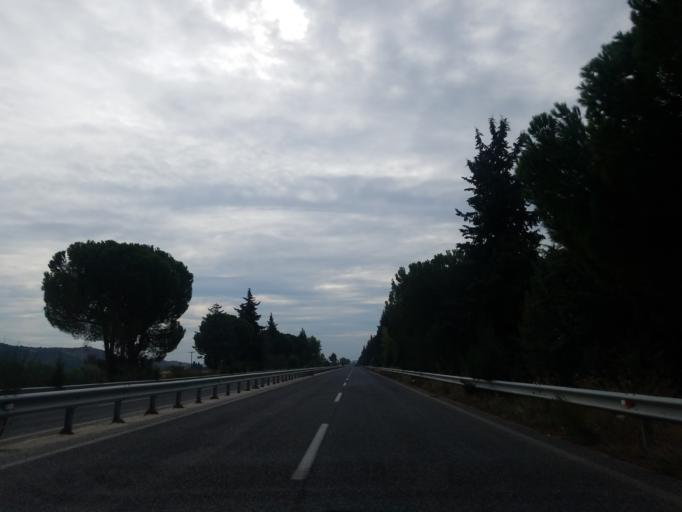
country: GR
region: Thessaly
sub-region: Trikala
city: Vasiliki
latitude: 39.6461
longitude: 21.6886
